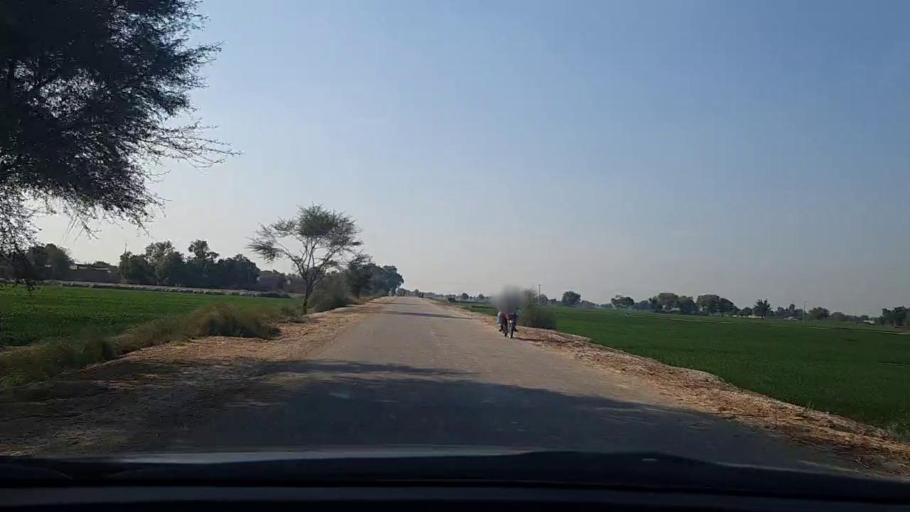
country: PK
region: Sindh
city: Daulatpur
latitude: 26.3172
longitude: 68.0591
